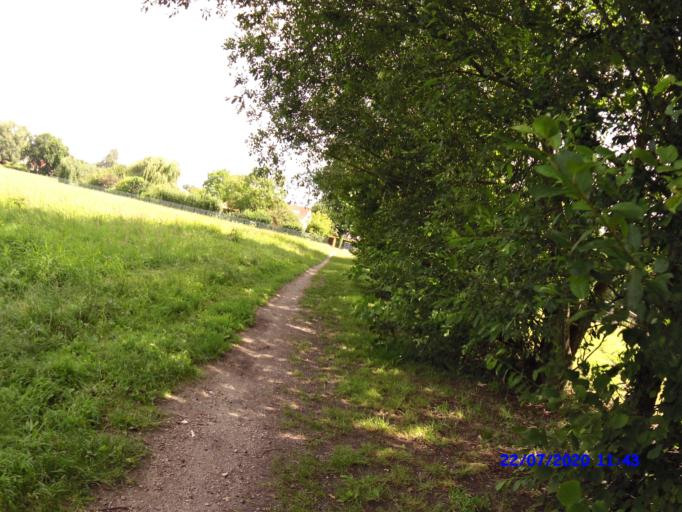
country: BE
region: Flanders
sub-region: Provincie Antwerpen
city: Berlaar
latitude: 51.0792
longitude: 4.6677
